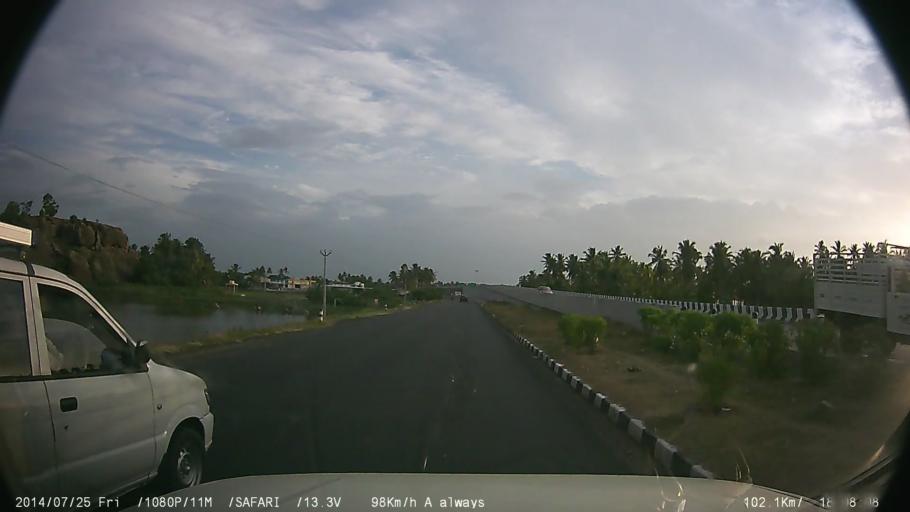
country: IN
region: Tamil Nadu
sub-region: Krishnagiri
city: Kaverippattanam
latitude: 12.4043
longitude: 78.2214
